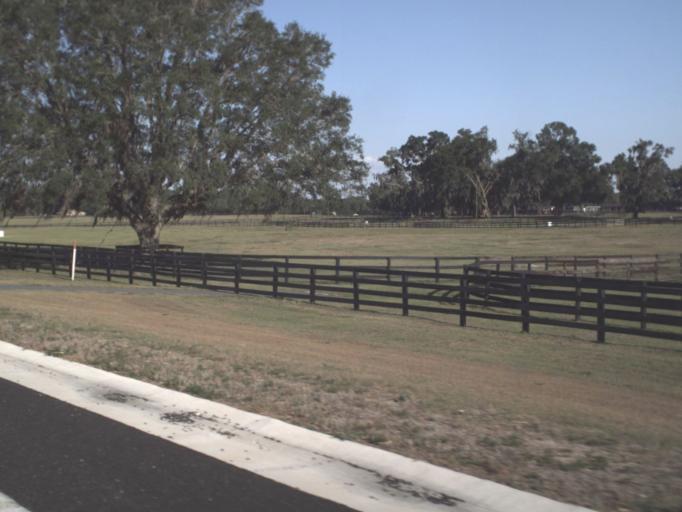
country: US
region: Florida
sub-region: Marion County
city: Ocala
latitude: 29.1866
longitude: -82.2583
